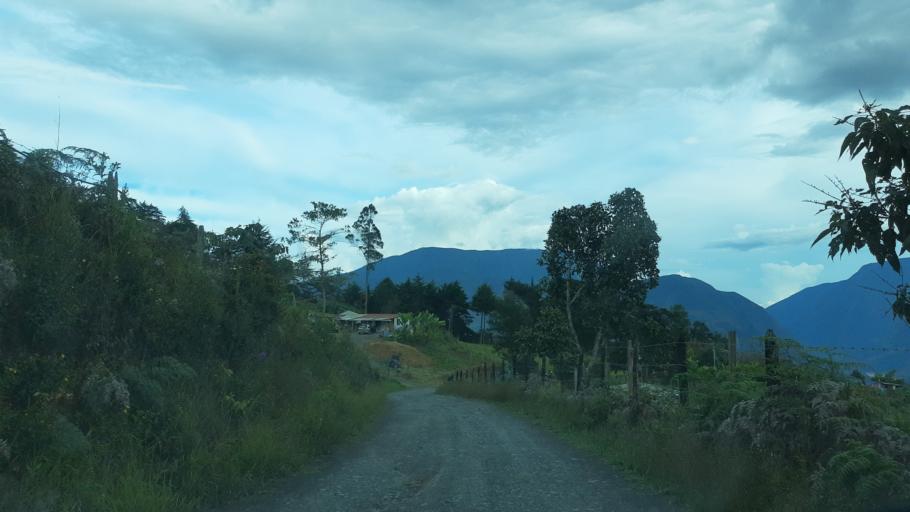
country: CO
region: Boyaca
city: Garagoa
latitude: 4.9876
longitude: -73.3313
